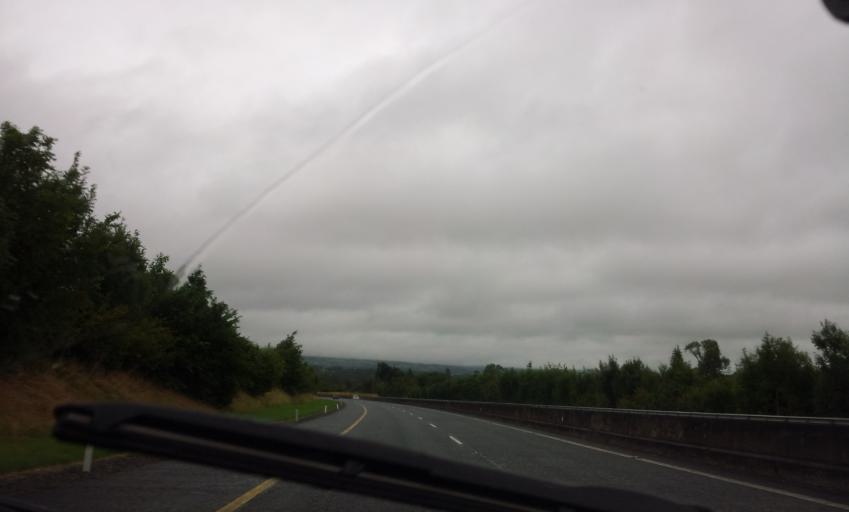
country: IE
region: Munster
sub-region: County Cork
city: Fermoy
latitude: 52.1294
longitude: -8.2602
